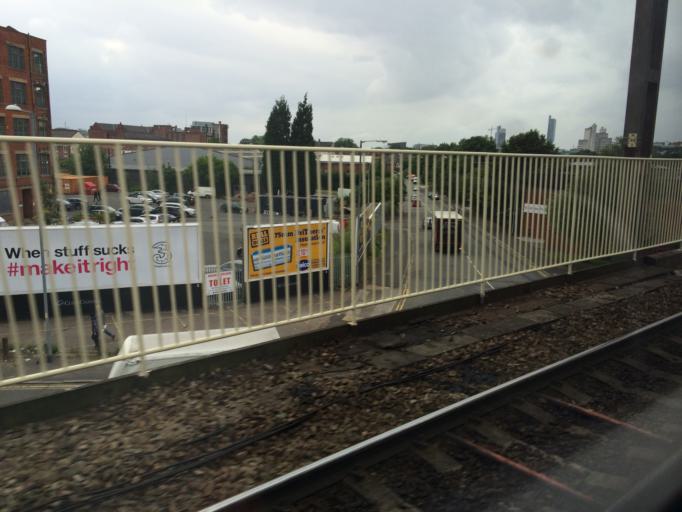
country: GB
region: England
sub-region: Manchester
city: Longsight
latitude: 53.4720
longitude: -2.2159
